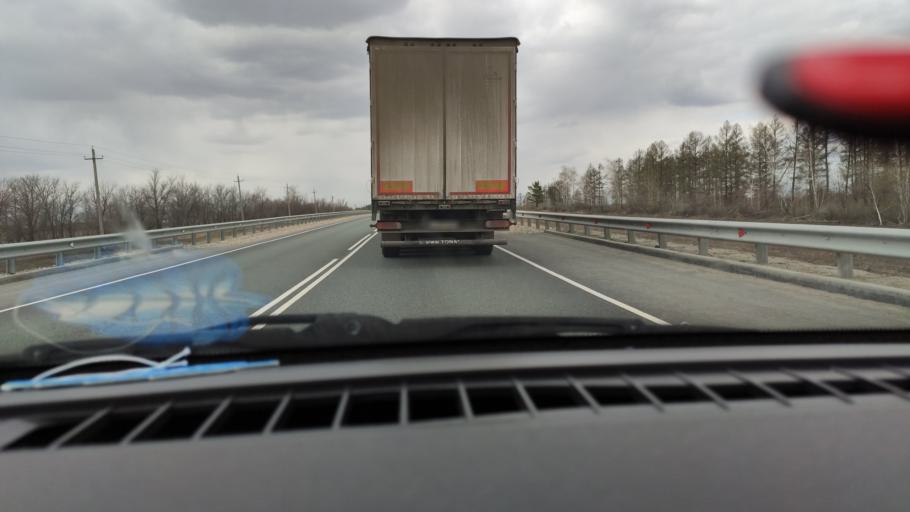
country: RU
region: Saratov
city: Shikhany
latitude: 52.1611
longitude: 47.1242
